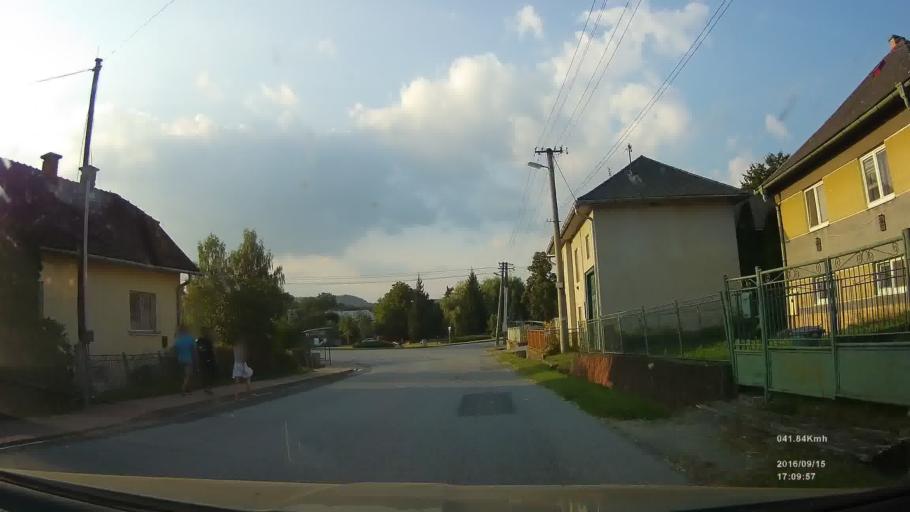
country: SK
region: Presovsky
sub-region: Okres Presov
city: Presov
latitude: 48.9175
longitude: 21.1191
